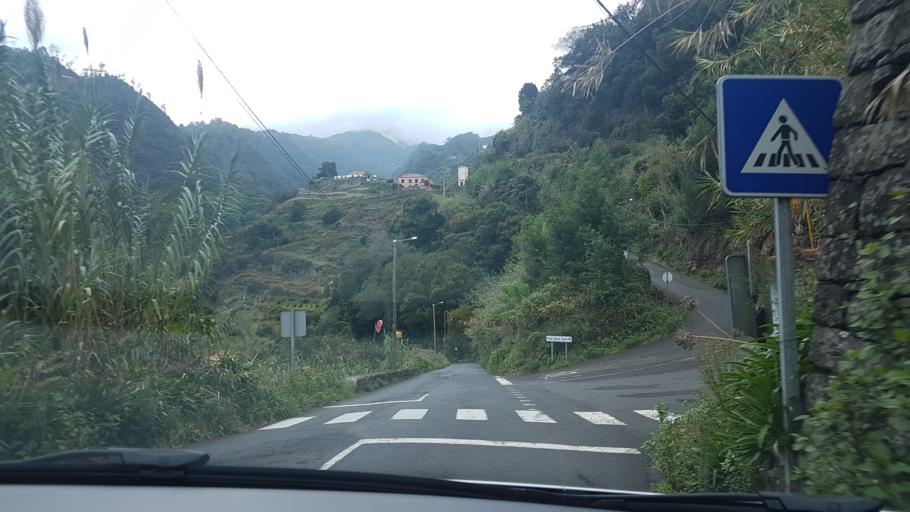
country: PT
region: Madeira
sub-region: Santana
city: Santana
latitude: 32.8210
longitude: -16.9002
